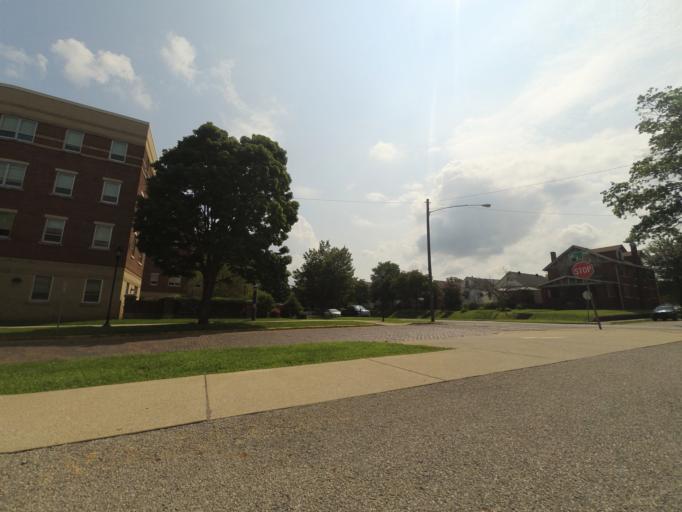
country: US
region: West Virginia
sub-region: Cabell County
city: Huntington
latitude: 38.4210
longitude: -82.4275
